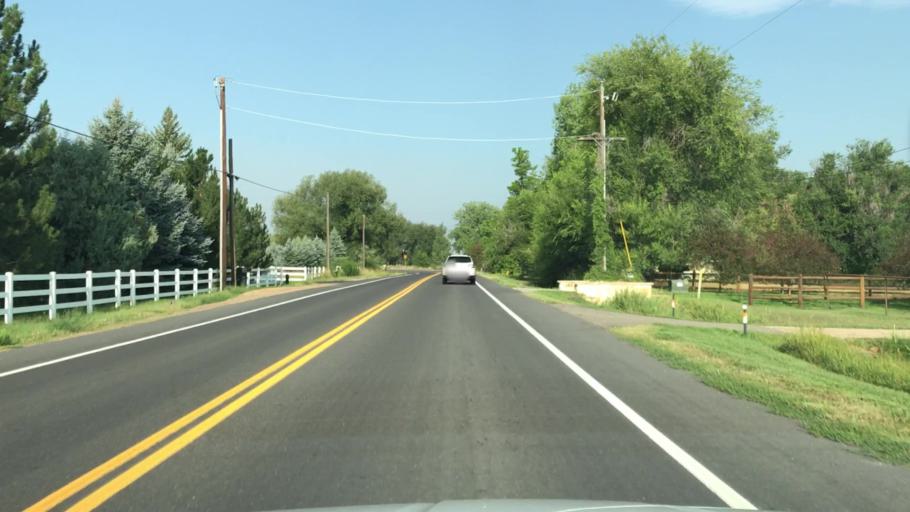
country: US
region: Colorado
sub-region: Boulder County
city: Gunbarrel
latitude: 40.0365
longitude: -105.1662
